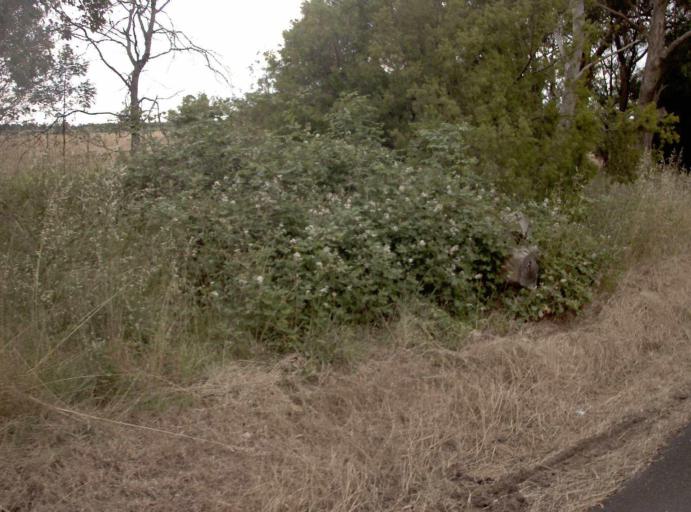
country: AU
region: Victoria
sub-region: Wellington
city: Sale
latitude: -38.3635
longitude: 146.9909
